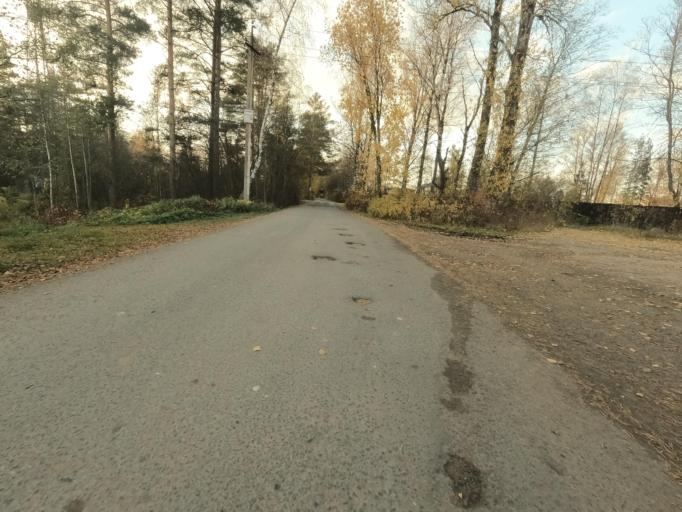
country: RU
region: St.-Petersburg
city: Beloostrov
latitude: 60.1613
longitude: 30.0044
